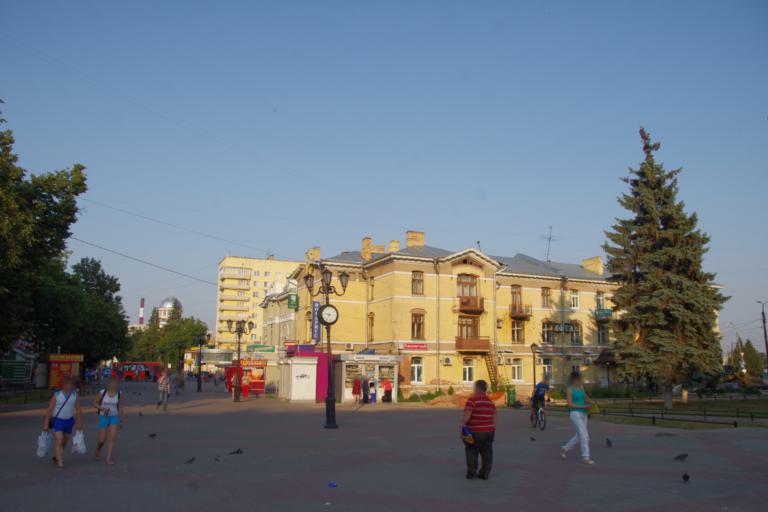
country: RU
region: Nizjnij Novgorod
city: Neklyudovo
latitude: 56.3496
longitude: 43.8662
